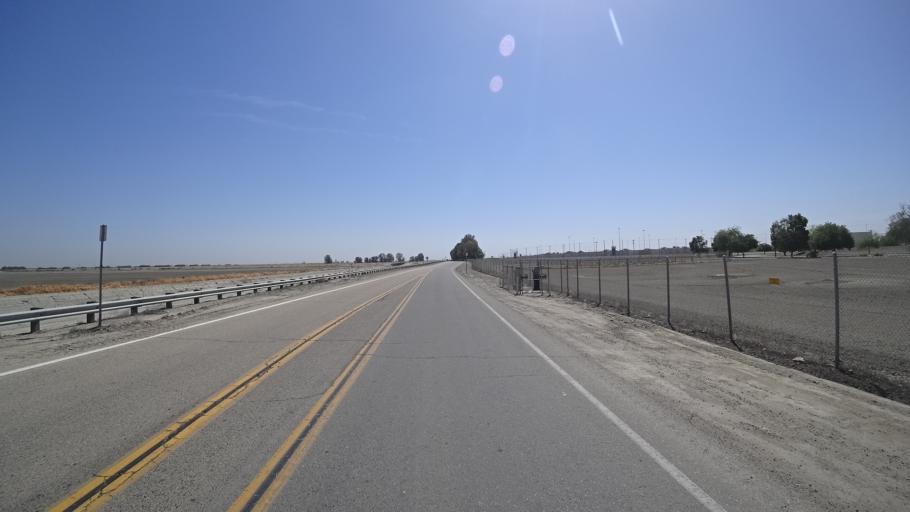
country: US
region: California
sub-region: Kings County
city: Corcoran
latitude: 36.0651
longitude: -119.5572
